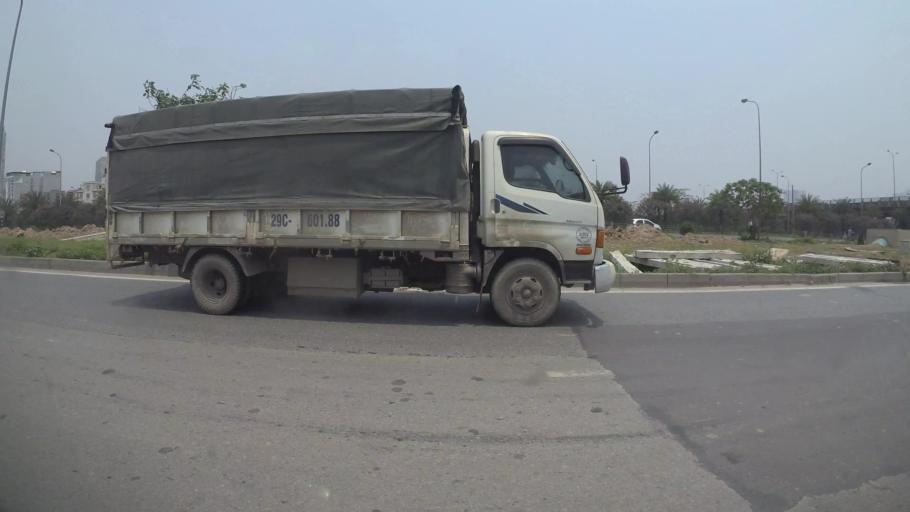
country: VN
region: Ha Noi
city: Thanh Xuan
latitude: 21.0020
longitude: 105.7813
